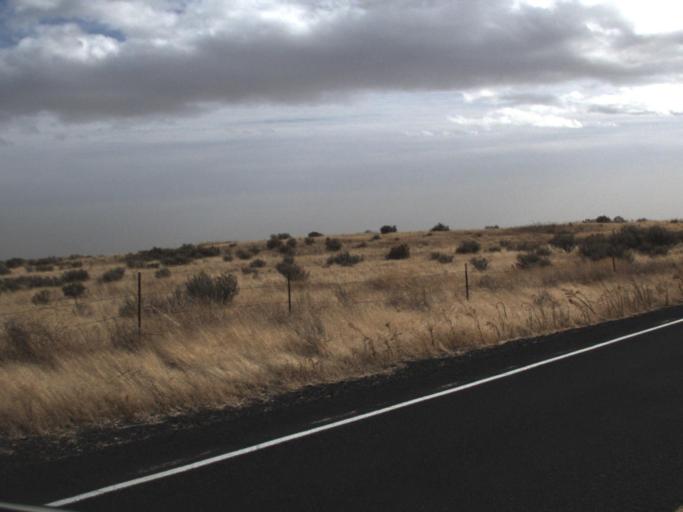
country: US
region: Washington
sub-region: Okanogan County
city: Coulee Dam
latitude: 47.5597
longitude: -118.7858
